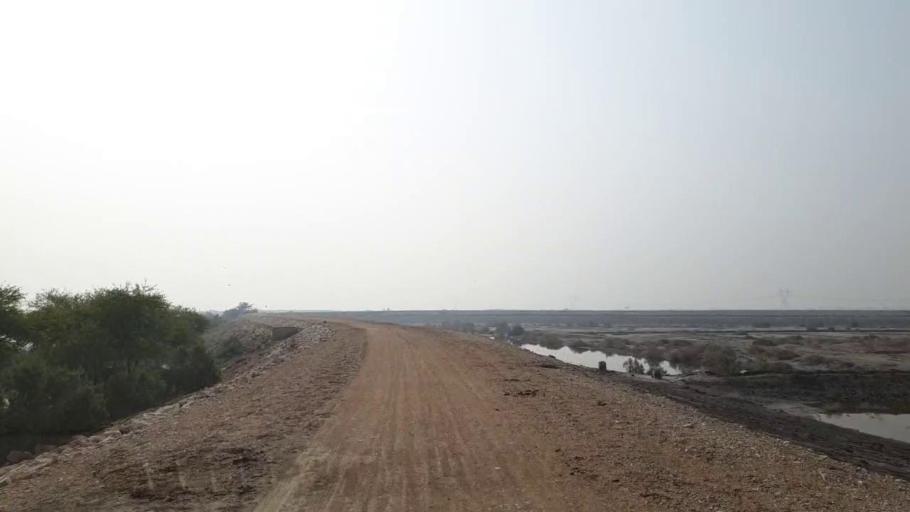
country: PK
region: Sindh
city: Sehwan
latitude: 26.4019
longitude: 67.8306
